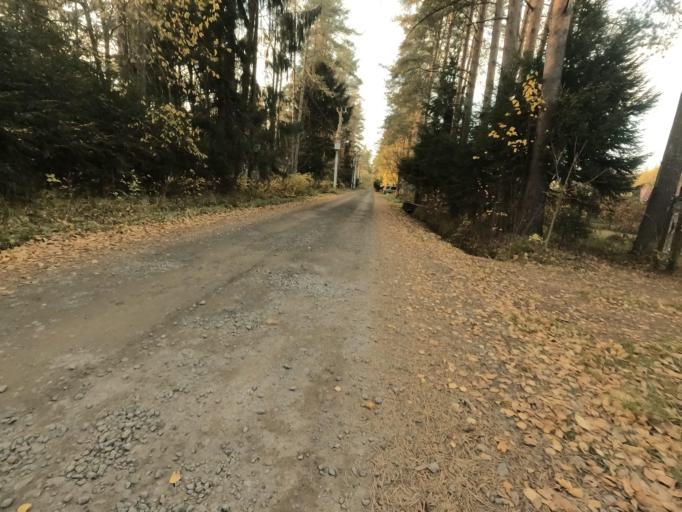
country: RU
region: St.-Petersburg
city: Beloostrov
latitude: 60.1704
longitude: 29.9853
